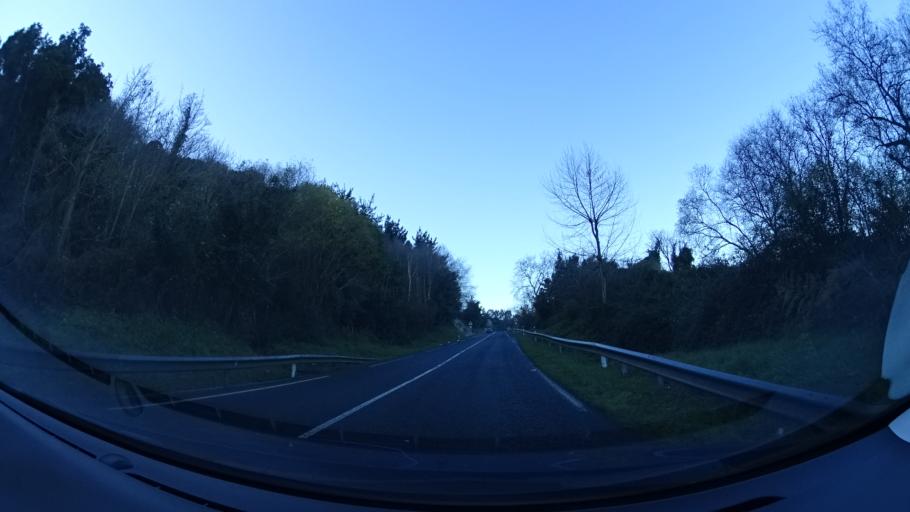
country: ES
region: Basque Country
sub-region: Provincia de Guipuzcoa
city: Deba
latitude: 43.3047
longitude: -2.3667
